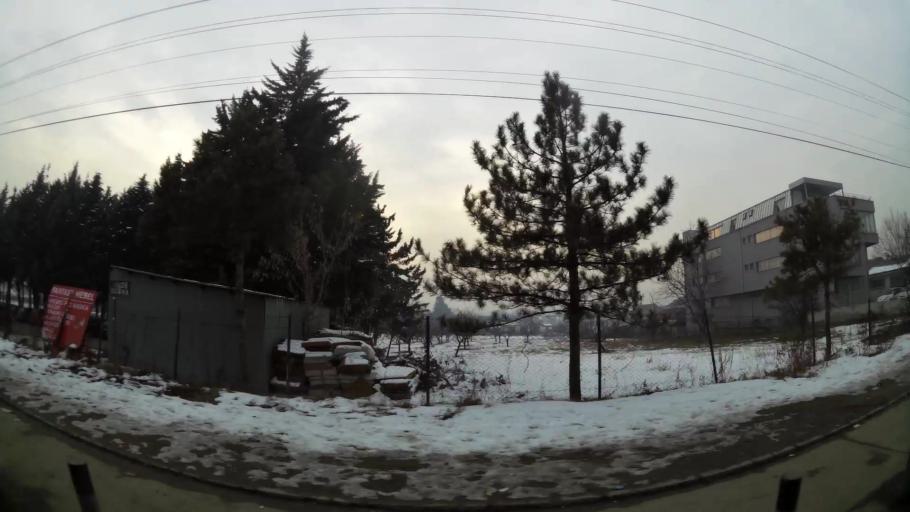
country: MK
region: Suto Orizari
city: Suto Orizare
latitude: 42.0322
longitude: 21.4280
